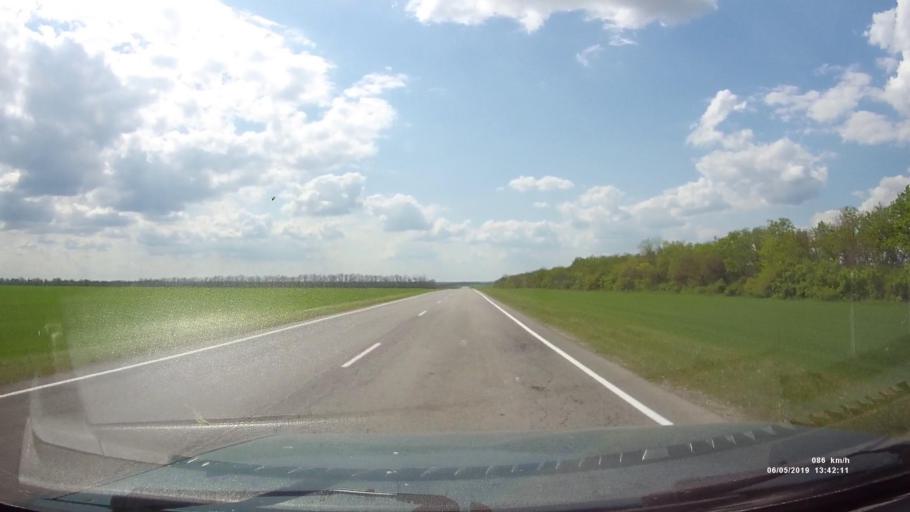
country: RU
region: Rostov
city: Semikarakorsk
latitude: 47.6594
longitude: 40.6609
